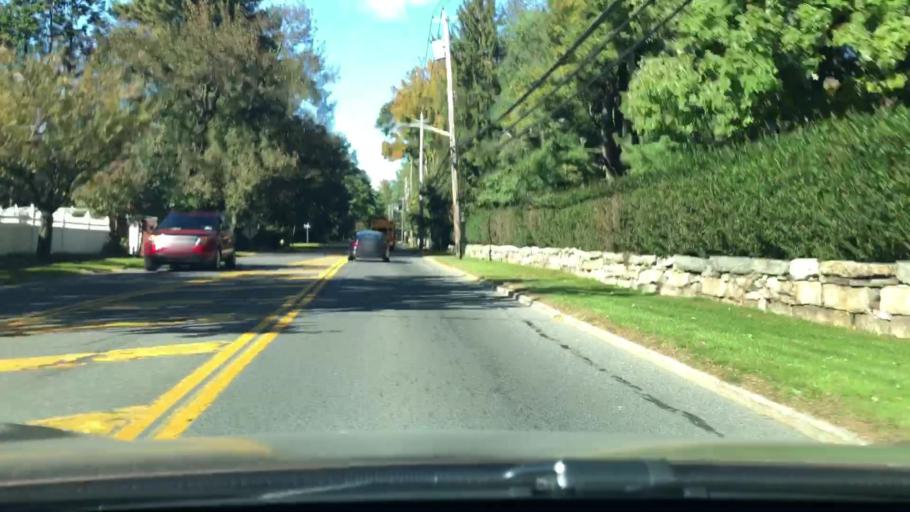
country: US
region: New York
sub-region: Westchester County
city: Harrison
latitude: 40.9888
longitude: -73.7102
